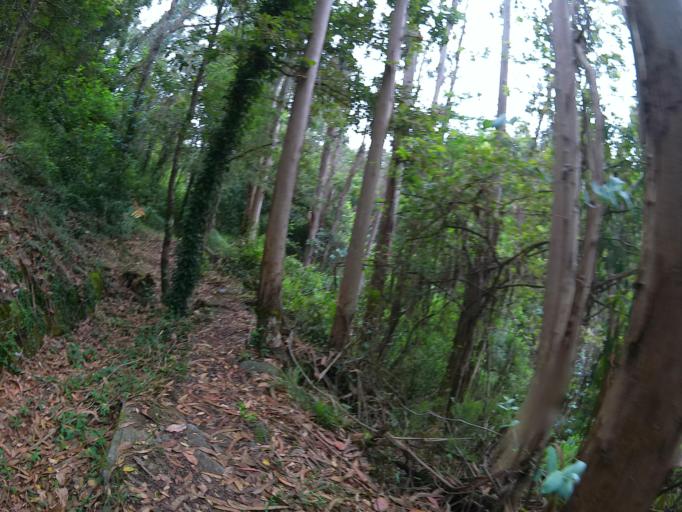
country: PT
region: Aveiro
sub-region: Albergaria-A-Velha
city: Branca
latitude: 40.7509
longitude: -8.4300
